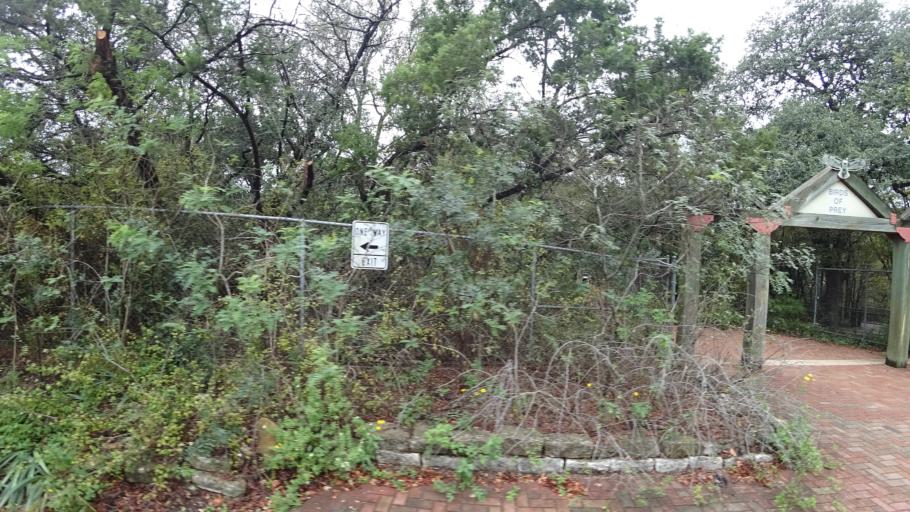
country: US
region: Texas
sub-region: Travis County
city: Rollingwood
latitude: 30.2717
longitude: -97.7758
